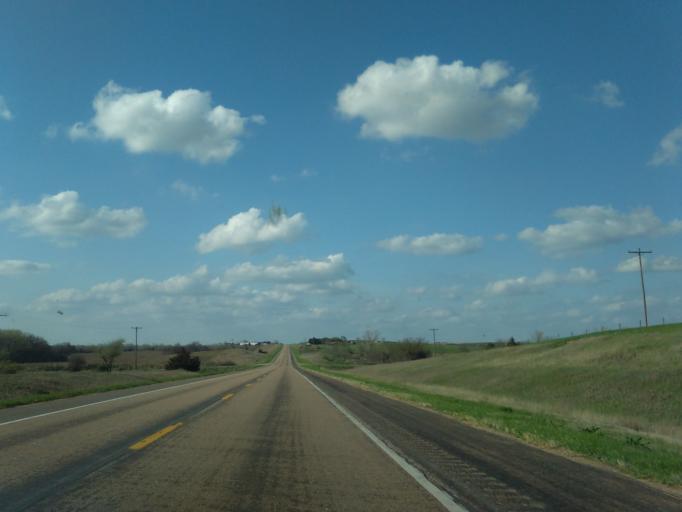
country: US
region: Nebraska
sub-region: Webster County
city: Red Cloud
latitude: 40.1298
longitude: -98.5189
